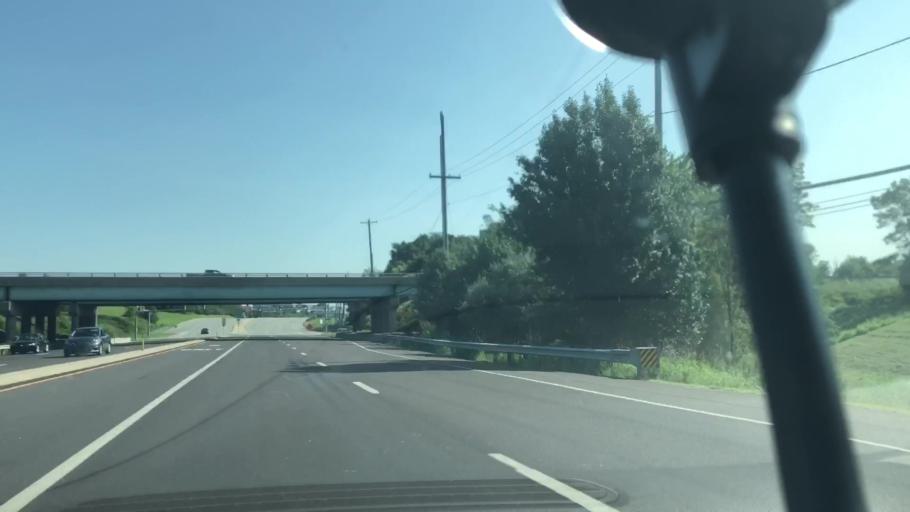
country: US
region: Pennsylvania
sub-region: Montgomery County
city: Collegeville
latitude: 40.1605
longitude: -75.4807
